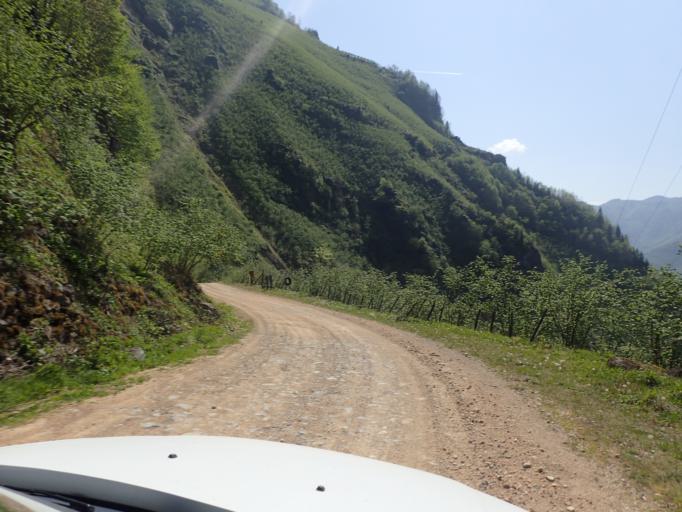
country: TR
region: Ordu
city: Kabaduz
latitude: 40.7466
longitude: 37.8830
